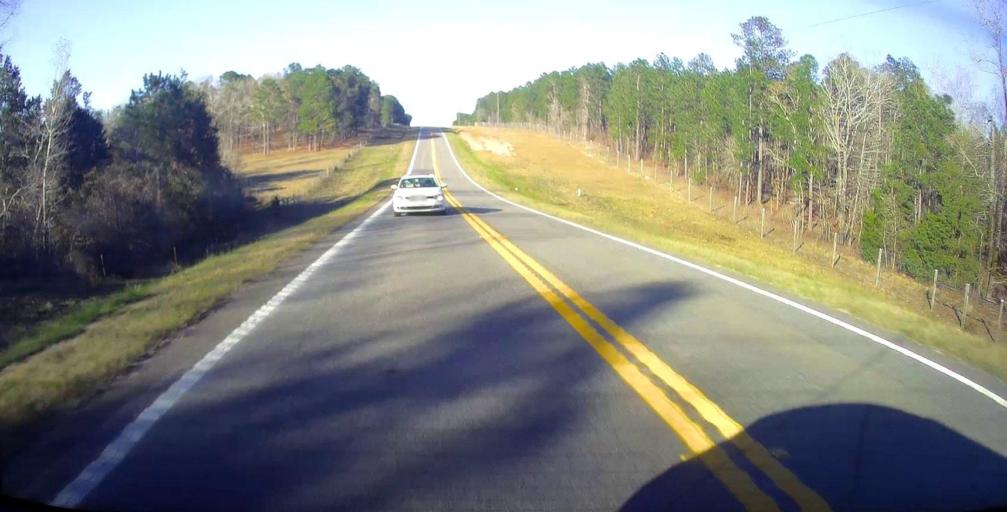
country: US
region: Georgia
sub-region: Taylor County
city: Butler
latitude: 32.4780
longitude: -84.3546
